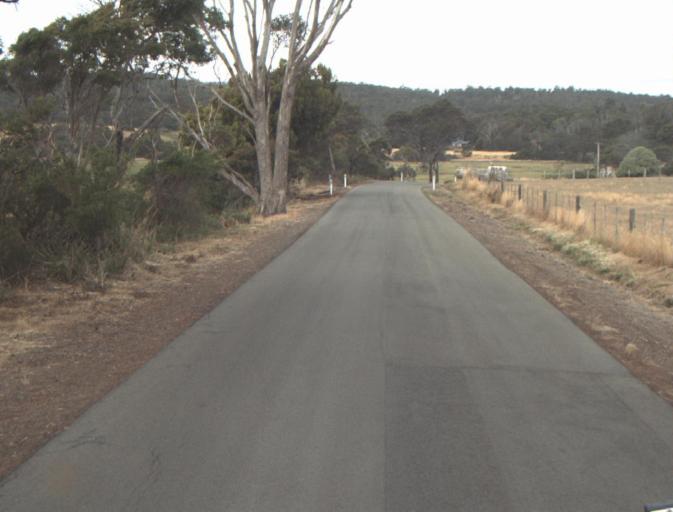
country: AU
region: Tasmania
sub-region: Launceston
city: Mayfield
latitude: -41.2831
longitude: 147.0080
